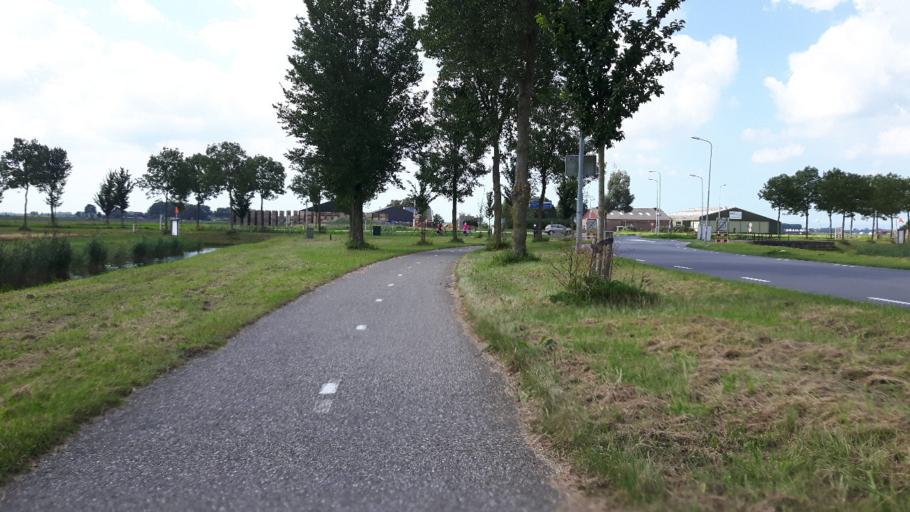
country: NL
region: North Holland
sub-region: Gemeente Medemblik
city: Medemblik
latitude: 52.7346
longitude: 5.1197
